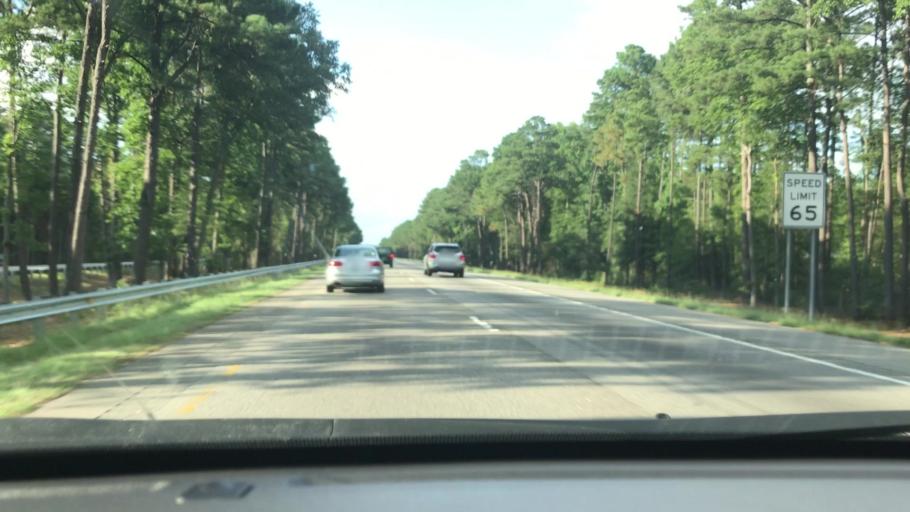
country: US
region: North Carolina
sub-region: Robeson County
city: Lumberton
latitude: 34.6833
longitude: -79.0015
